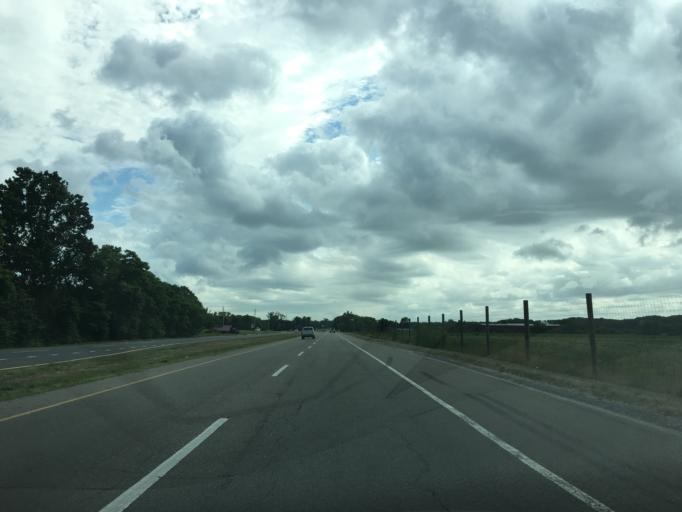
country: US
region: New York
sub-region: Suffolk County
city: Southold
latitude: 41.0595
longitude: -72.4479
